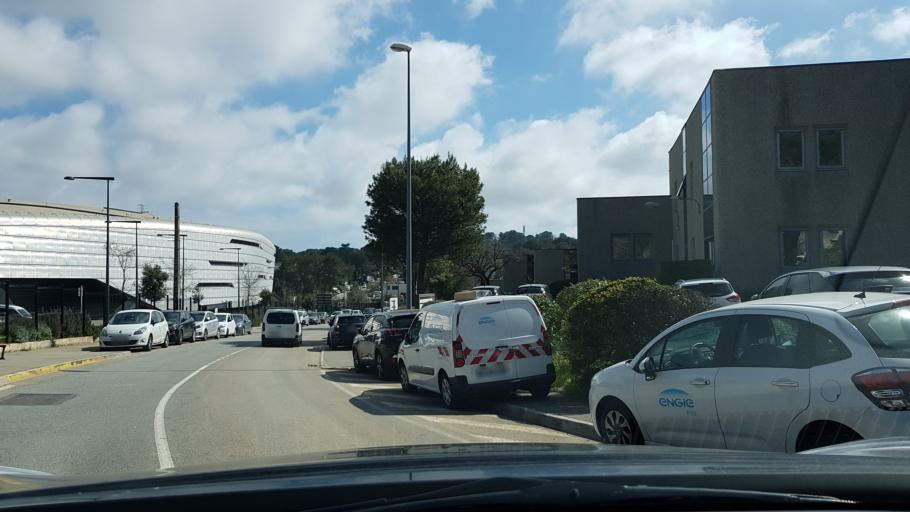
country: FR
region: Provence-Alpes-Cote d'Azur
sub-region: Departement des Alpes-Maritimes
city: Biot
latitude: 43.6070
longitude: 7.0754
